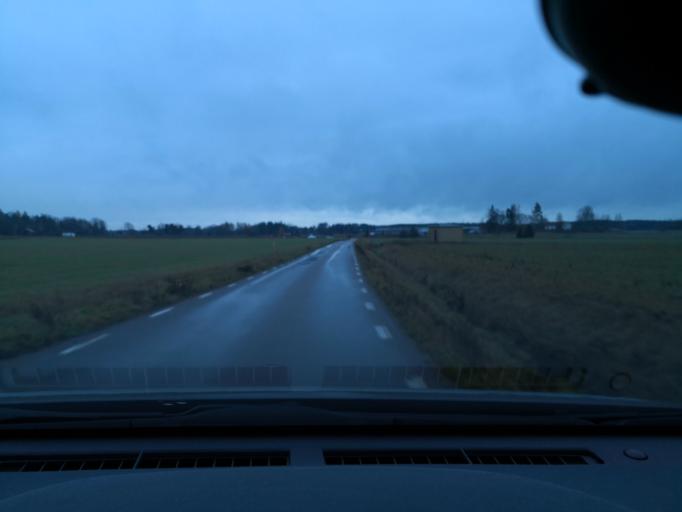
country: SE
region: Vaestmanland
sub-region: Hallstahammars Kommun
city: Kolback
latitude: 59.5636
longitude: 16.2014
